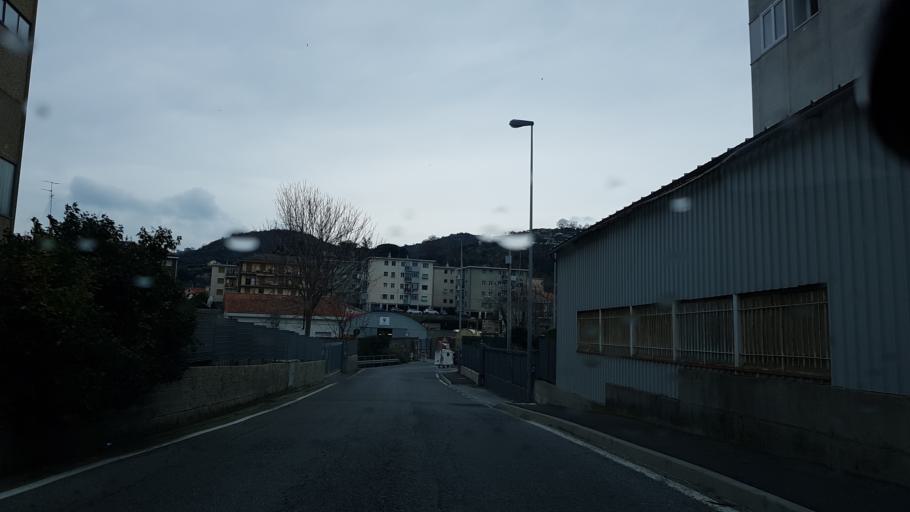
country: IT
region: Liguria
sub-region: Provincia di Savona
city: Savona
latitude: 44.3020
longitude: 8.4520
